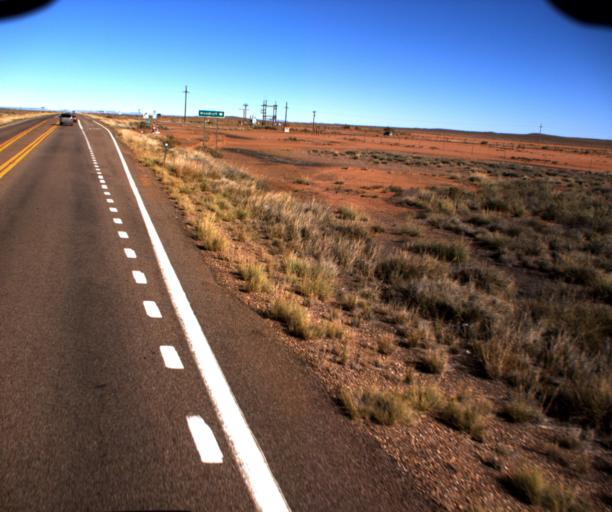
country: US
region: Arizona
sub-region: Navajo County
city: Holbrook
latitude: 34.7958
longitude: -110.1341
